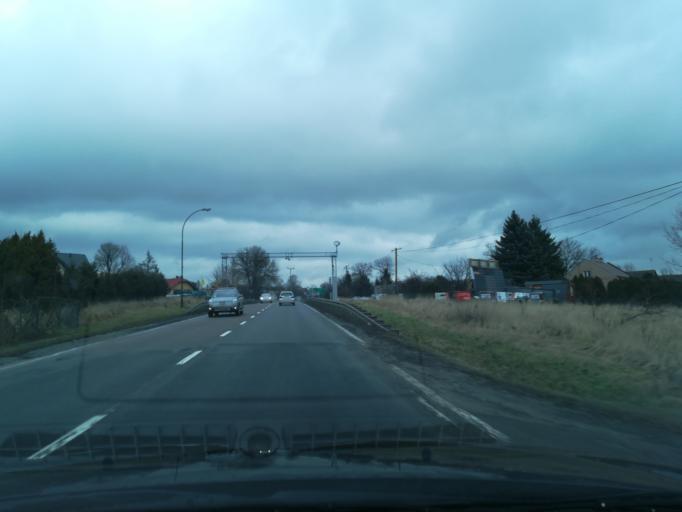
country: PL
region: Subcarpathian Voivodeship
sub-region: Powiat lancucki
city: Lancut
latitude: 50.0715
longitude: 22.2480
